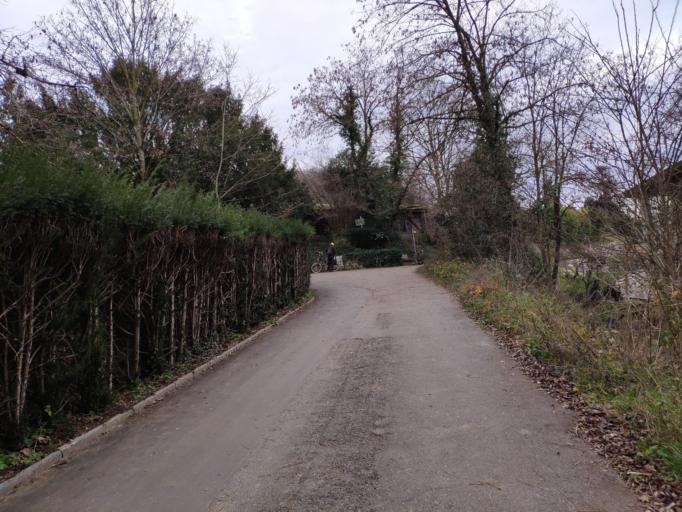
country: CH
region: Basel-City
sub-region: Basel-Stadt
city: Riehen
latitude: 47.5616
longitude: 7.6407
